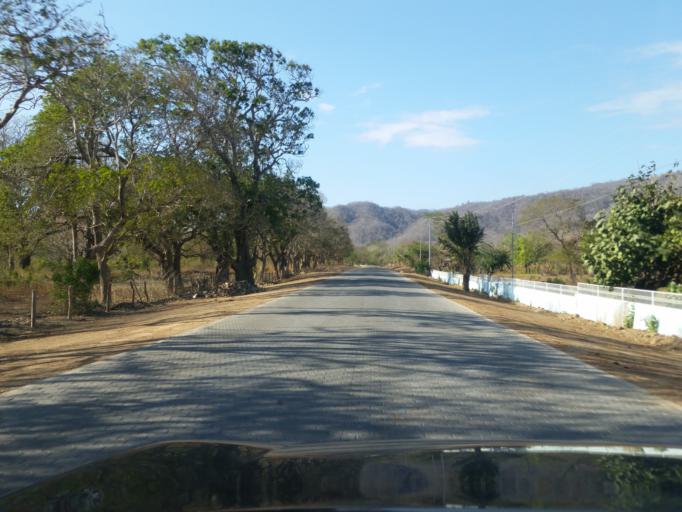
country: NI
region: Rivas
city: Tola
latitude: 11.4162
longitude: -86.0088
